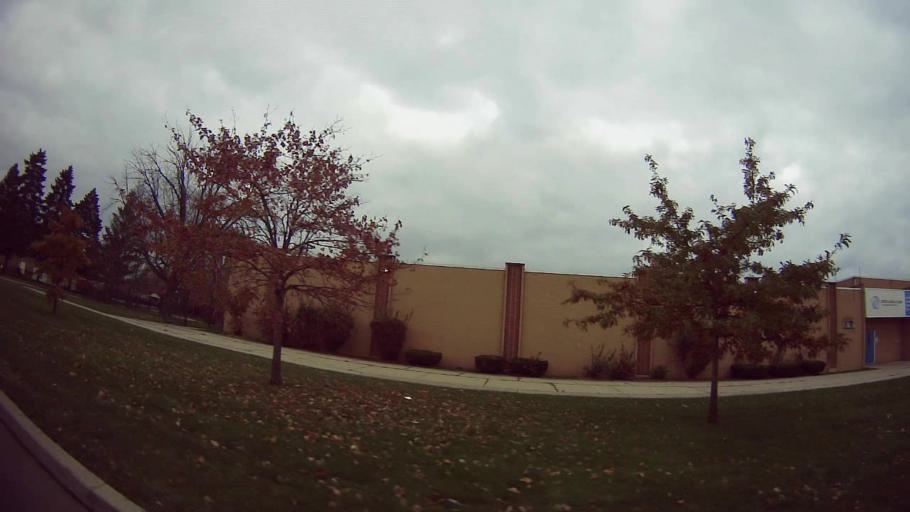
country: US
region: Michigan
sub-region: Macomb County
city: Eastpointe
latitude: 42.4455
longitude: -82.9854
